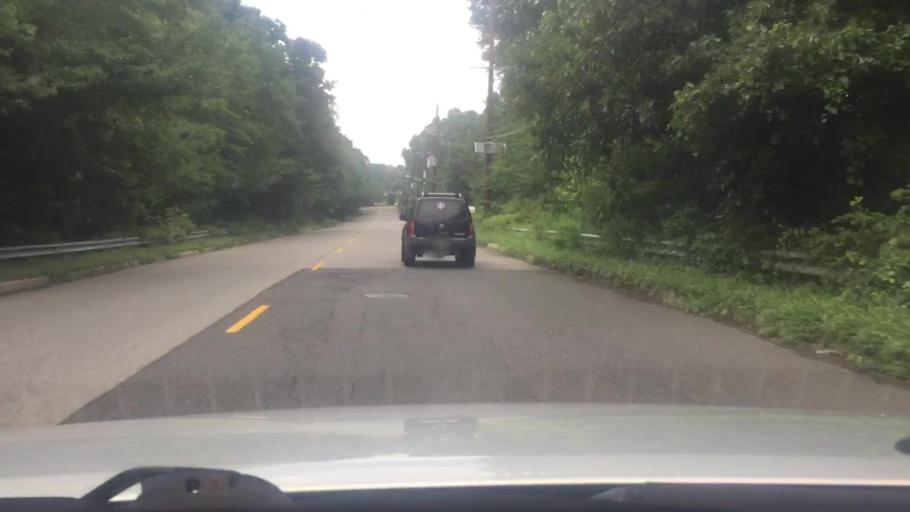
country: US
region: New Jersey
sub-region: Middlesex County
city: South River
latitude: 40.4523
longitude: -74.4092
